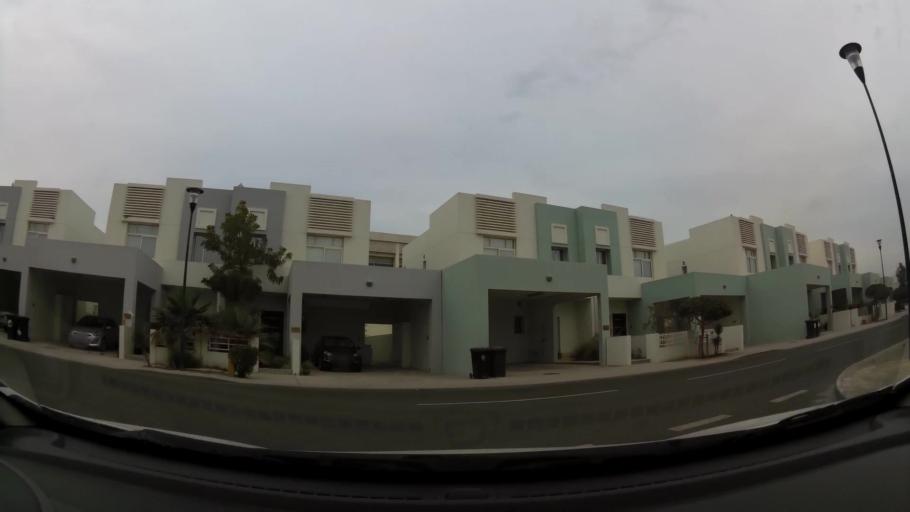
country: BH
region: Northern
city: Ar Rifa'
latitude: 26.1002
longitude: 50.5625
